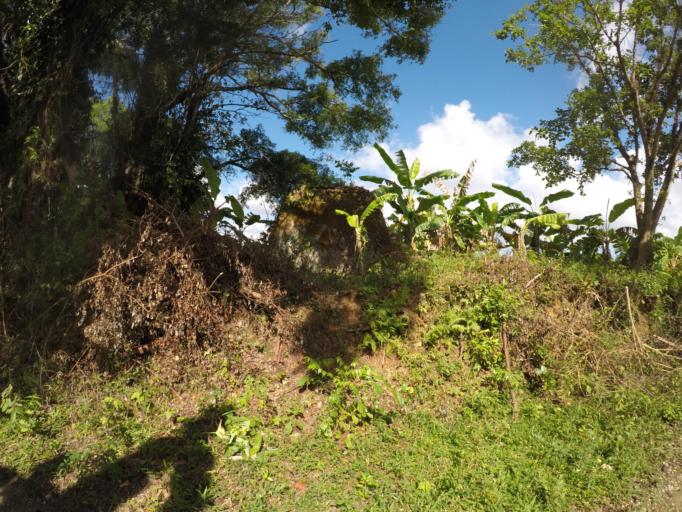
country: TZ
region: Pemba South
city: Mtambile
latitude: -5.3477
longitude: 39.6904
